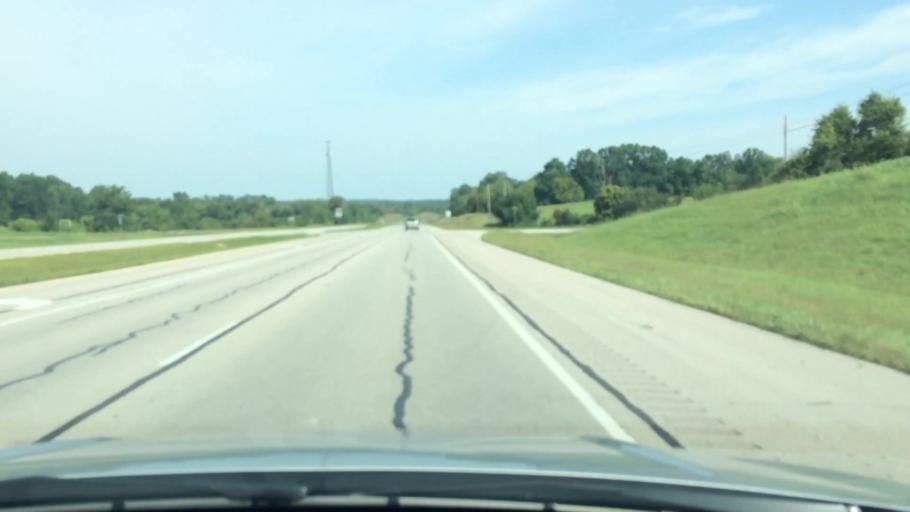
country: US
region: Kentucky
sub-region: Anderson County
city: Lawrenceburg
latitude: 38.0865
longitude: -84.9185
